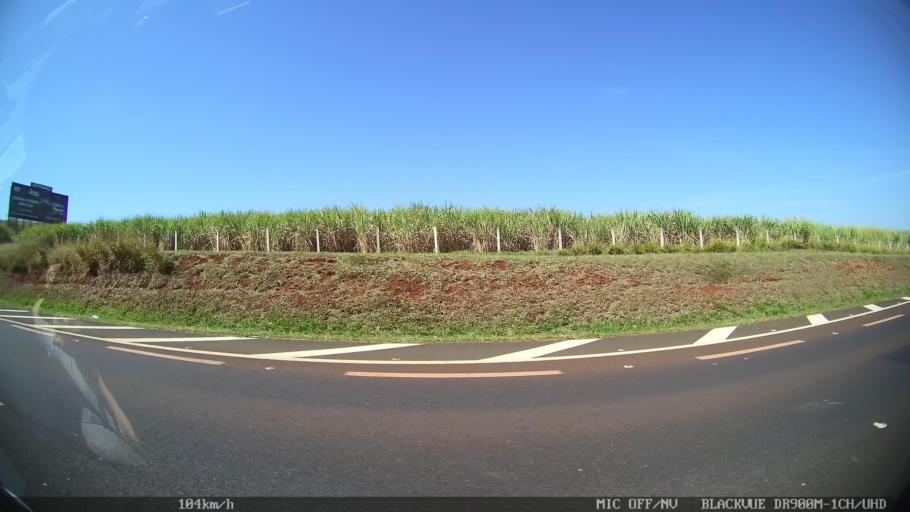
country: BR
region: Sao Paulo
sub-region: Batatais
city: Batatais
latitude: -20.7830
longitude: -47.5523
